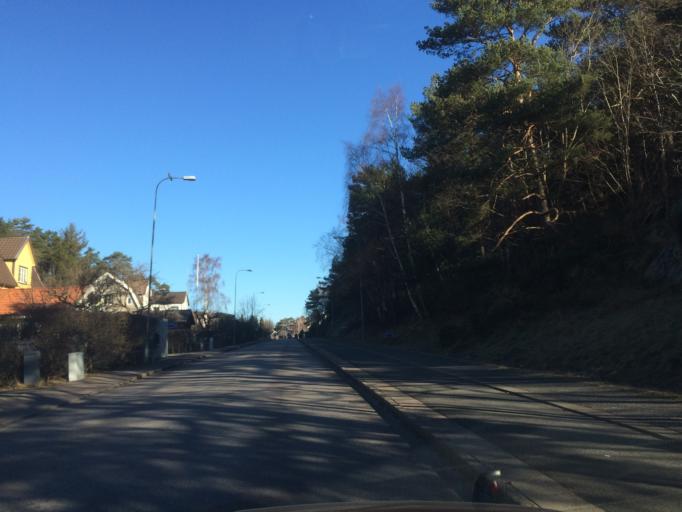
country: SE
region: Vaestra Goetaland
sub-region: Goteborg
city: Majorna
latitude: 57.6675
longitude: 11.8973
